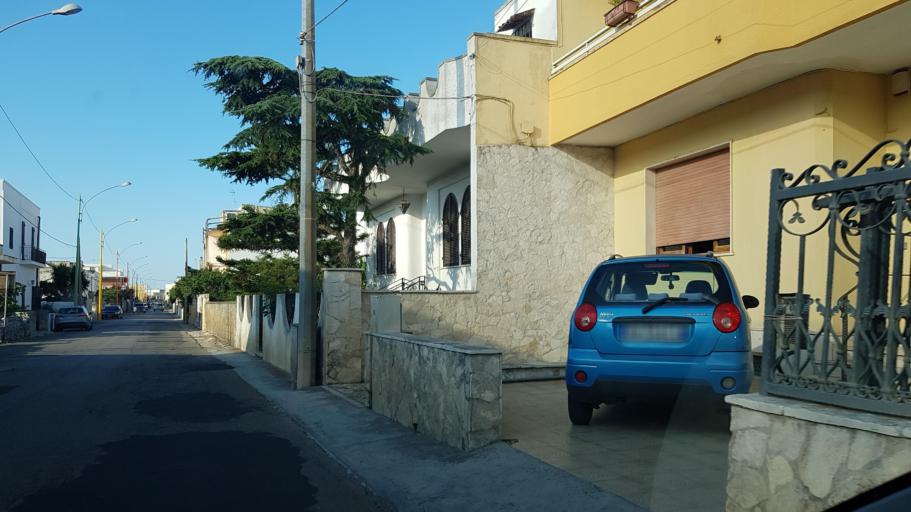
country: IT
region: Apulia
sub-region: Provincia di Lecce
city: Andrano
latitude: 39.9836
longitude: 18.3792
